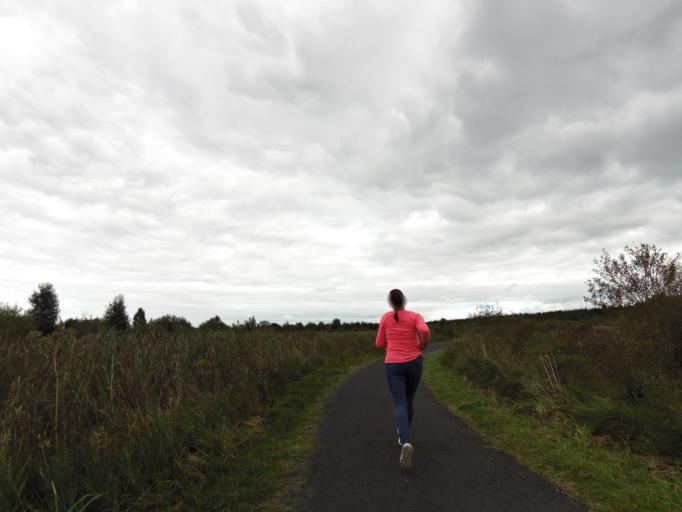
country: IE
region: Leinster
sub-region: Uibh Fhaili
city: Ferbane
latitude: 53.2218
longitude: -7.7497
